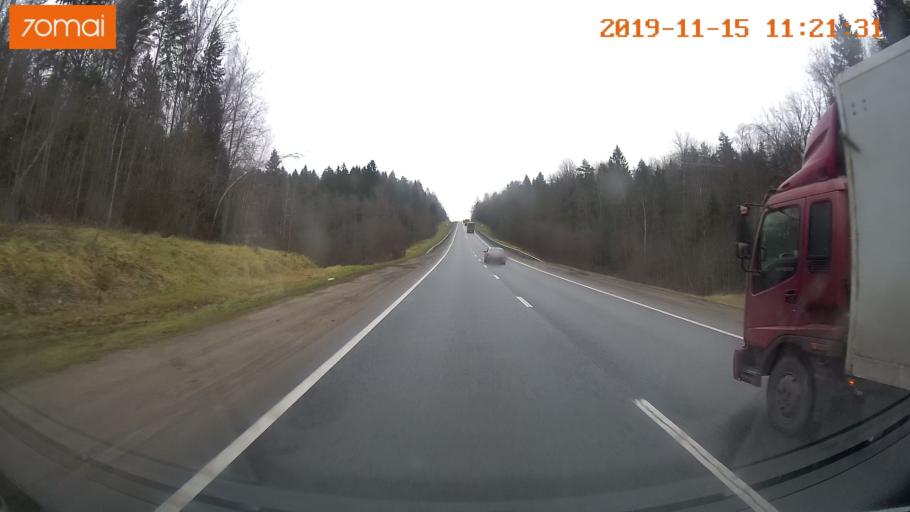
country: RU
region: Vologda
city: Molochnoye
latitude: 59.1447
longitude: 39.3393
